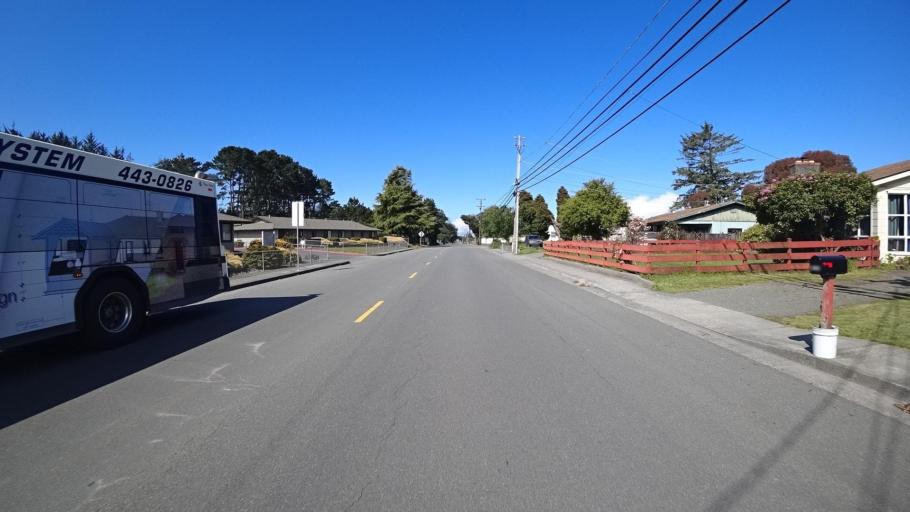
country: US
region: California
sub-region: Humboldt County
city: McKinleyville
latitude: 40.9465
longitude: -124.1024
